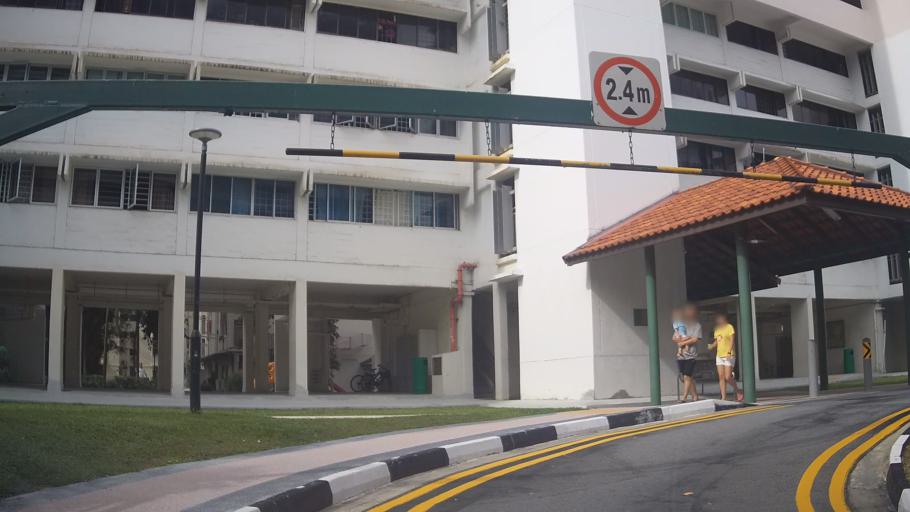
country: SG
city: Singapore
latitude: 1.3235
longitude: 103.8620
